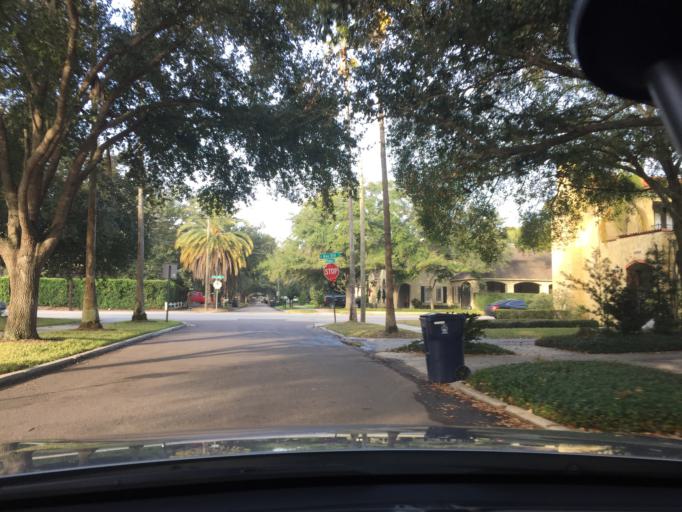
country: US
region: Florida
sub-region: Hillsborough County
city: Tampa
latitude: 27.9369
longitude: -82.4929
